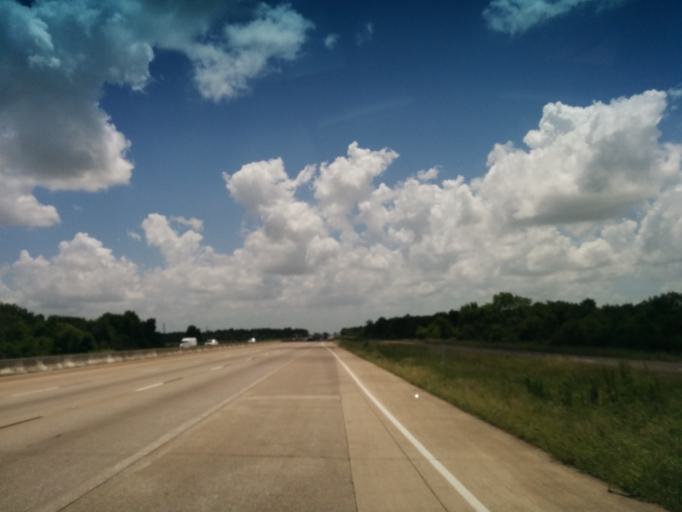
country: US
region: Texas
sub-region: Chambers County
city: Anahuac
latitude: 29.8381
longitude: -94.5999
